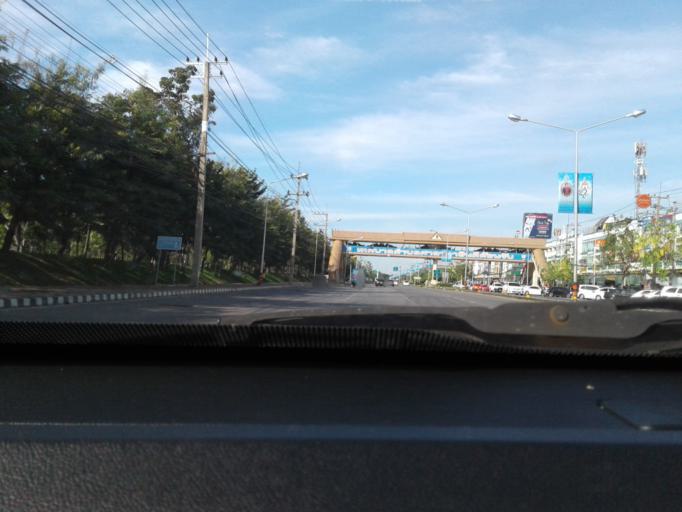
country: TH
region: Bangkok
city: Thawi Watthana
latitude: 13.7948
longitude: 100.3273
